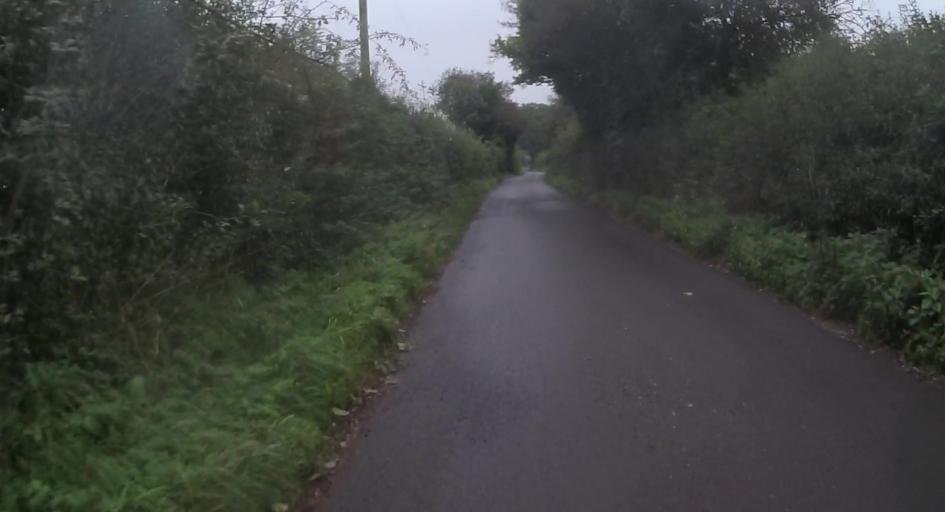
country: GB
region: England
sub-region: West Berkshire
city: Thatcham
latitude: 51.4109
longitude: -1.2136
